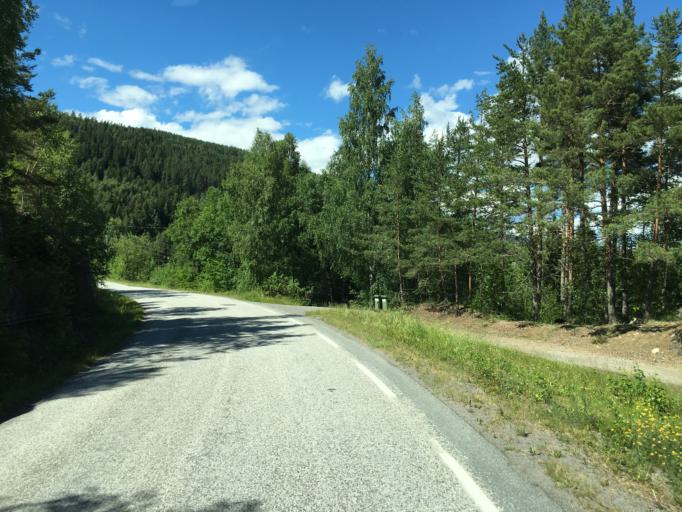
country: NO
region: Oppland
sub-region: Jevnaker
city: Jevnaker
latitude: 60.3096
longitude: 10.3468
